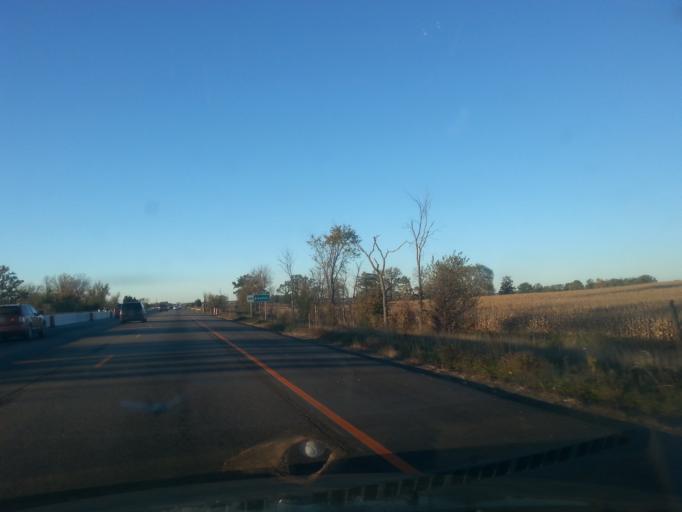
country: CA
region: Ontario
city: Bradford West Gwillimbury
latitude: 44.0764
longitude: -79.6250
